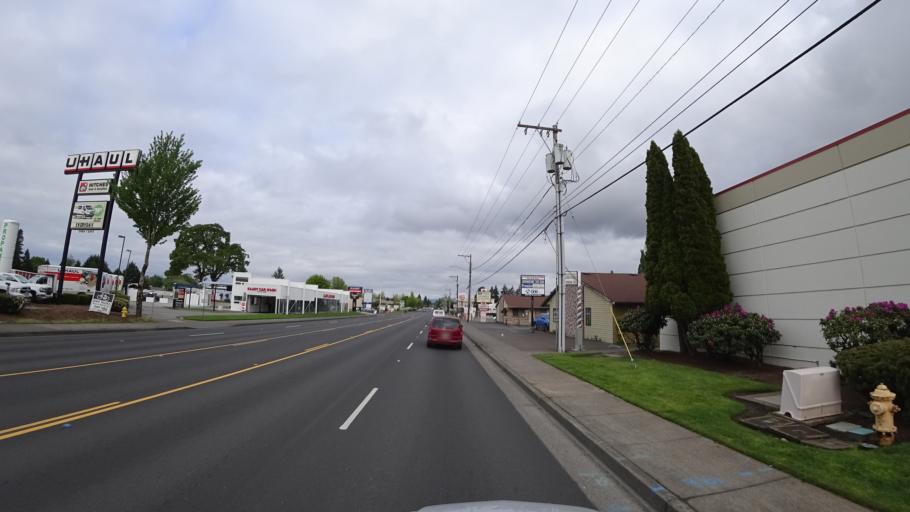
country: US
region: Oregon
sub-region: Washington County
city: Hillsboro
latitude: 45.5307
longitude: -122.9586
